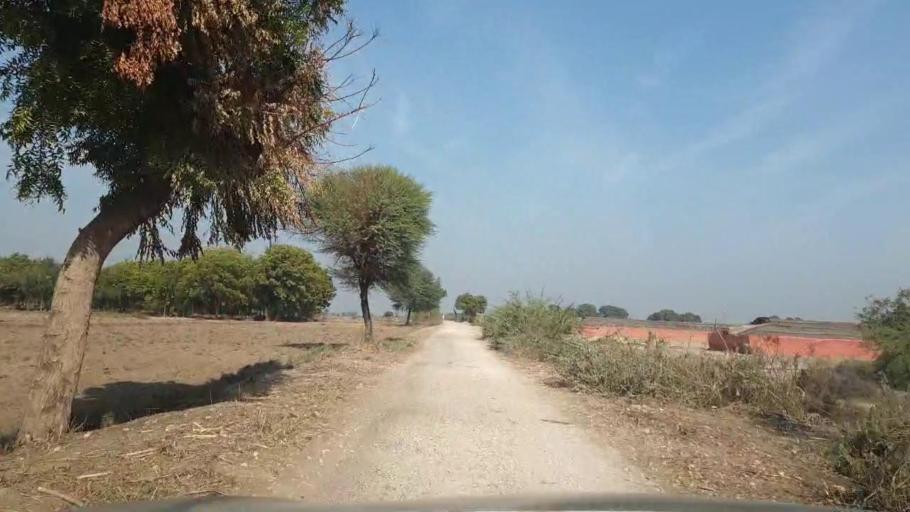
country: PK
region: Sindh
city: Tando Adam
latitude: 25.6415
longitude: 68.7284
